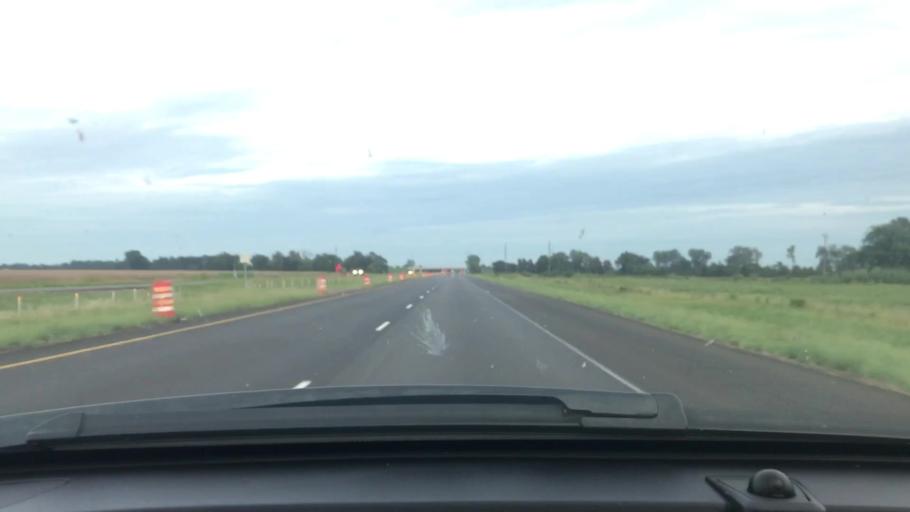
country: US
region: Arkansas
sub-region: Poinsett County
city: Trumann
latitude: 35.6513
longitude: -90.5287
